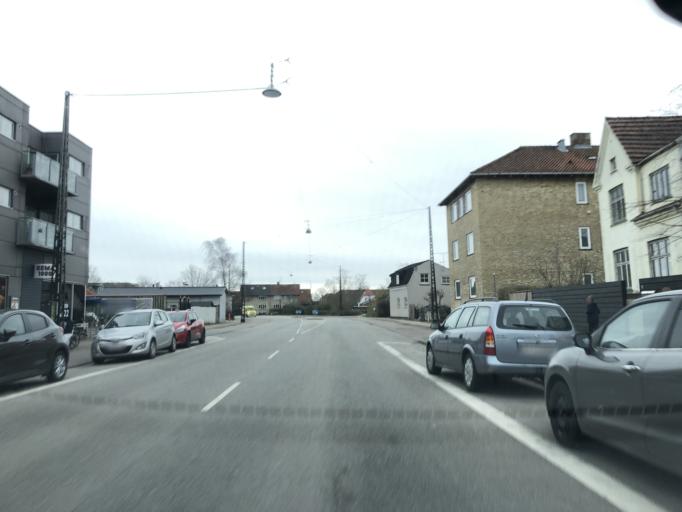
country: DK
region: Capital Region
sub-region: Tarnby Kommune
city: Tarnby
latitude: 55.6490
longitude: 12.6214
